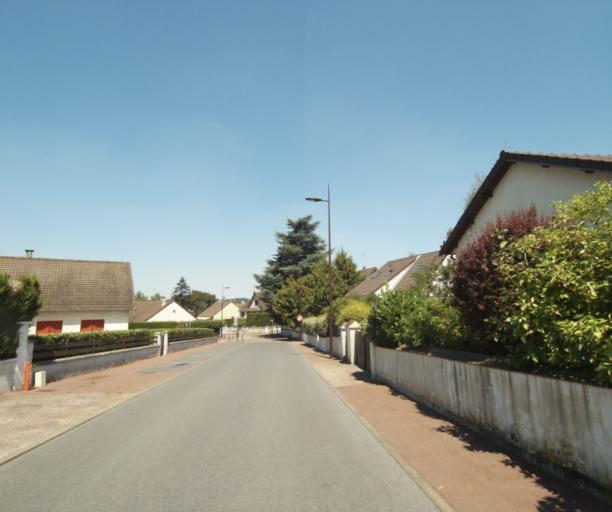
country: FR
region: Ile-de-France
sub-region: Departement de Seine-et-Marne
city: Lagny-sur-Marne
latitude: 48.8752
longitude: 2.7291
